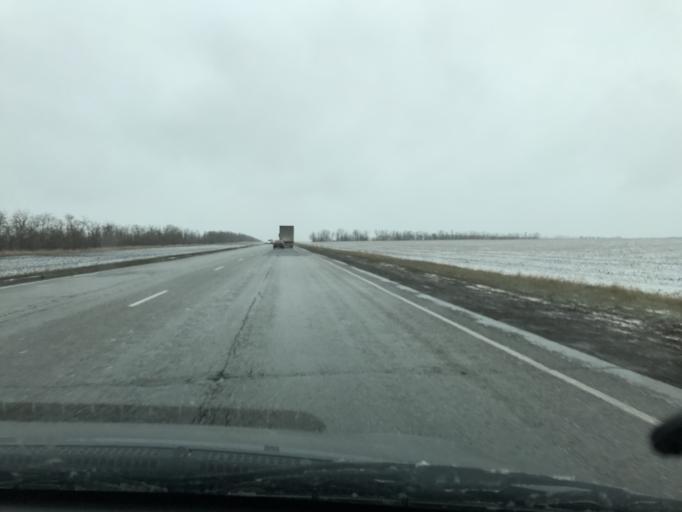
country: RU
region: Rostov
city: Kagal'nitskaya
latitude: 46.8675
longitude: 40.1732
